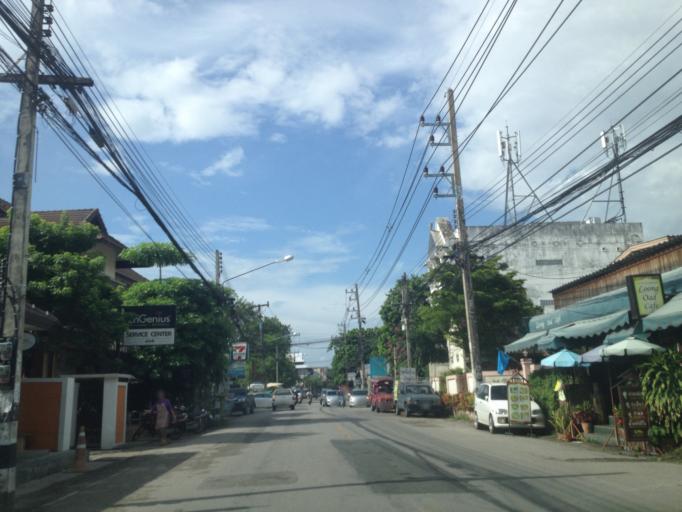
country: TH
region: Chiang Mai
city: Chiang Mai
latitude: 18.7832
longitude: 98.9818
